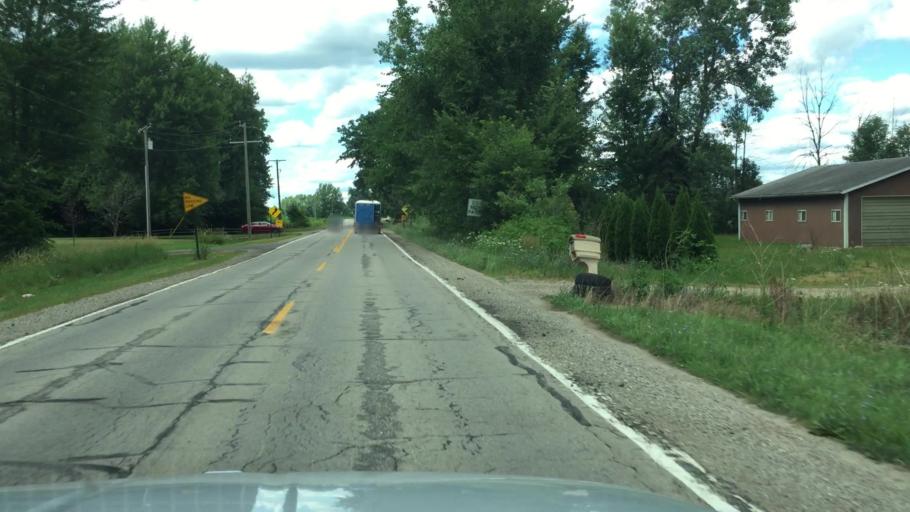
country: US
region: Michigan
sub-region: Saint Clair County
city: Capac
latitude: 42.9403
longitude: -82.9460
